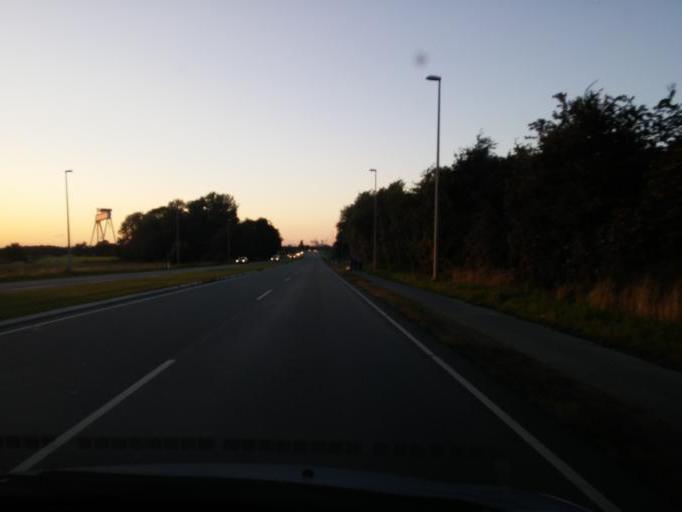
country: DK
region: South Denmark
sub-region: Kerteminde Kommune
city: Munkebo
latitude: 55.4529
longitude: 10.5405
